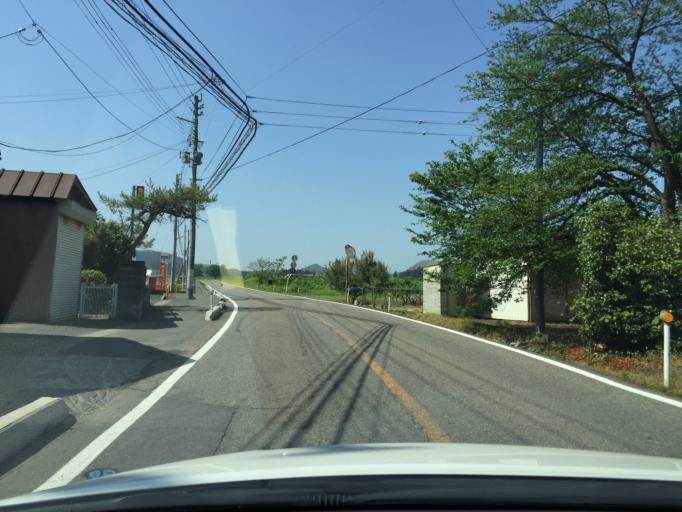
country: JP
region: Niigata
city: Muramatsu
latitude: 37.6821
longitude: 139.1505
